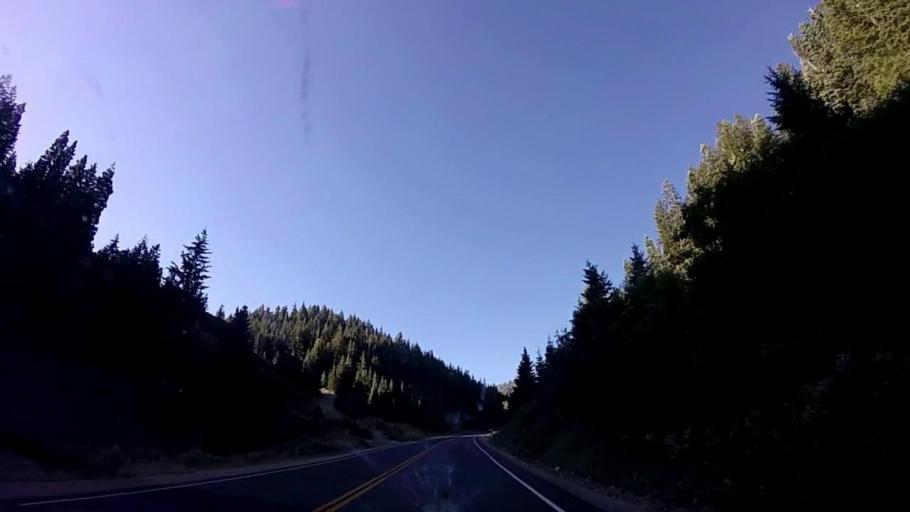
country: US
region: Utah
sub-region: Summit County
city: Park City
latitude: 40.6325
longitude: -111.4951
